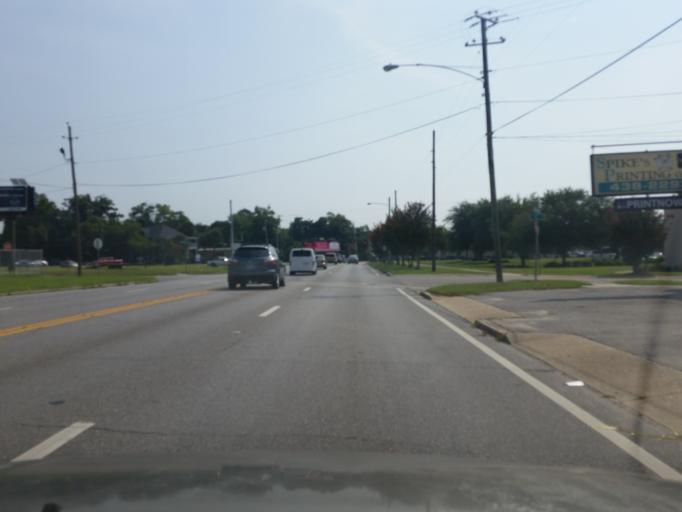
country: US
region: Florida
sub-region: Escambia County
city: Pensacola
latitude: 30.4102
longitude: -87.2310
